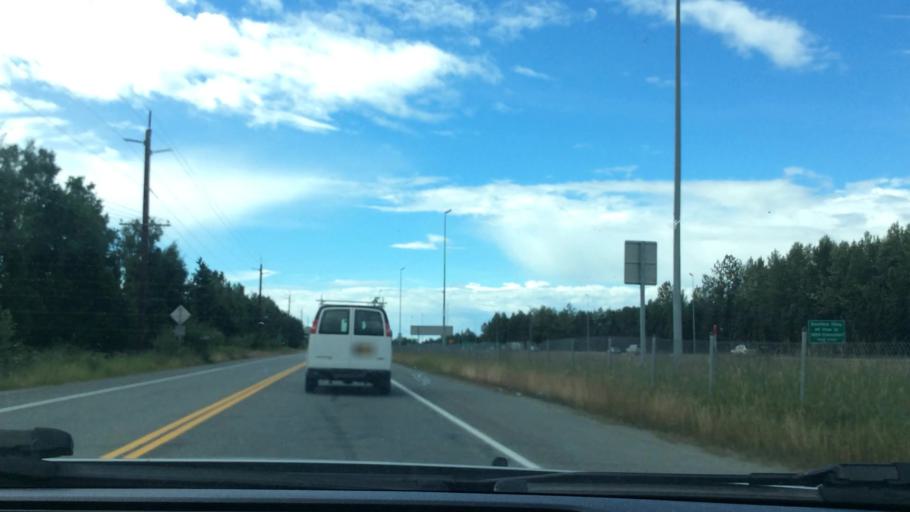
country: US
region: Alaska
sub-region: Anchorage Municipality
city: Elmendorf Air Force Base
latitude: 61.2242
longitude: -149.7593
